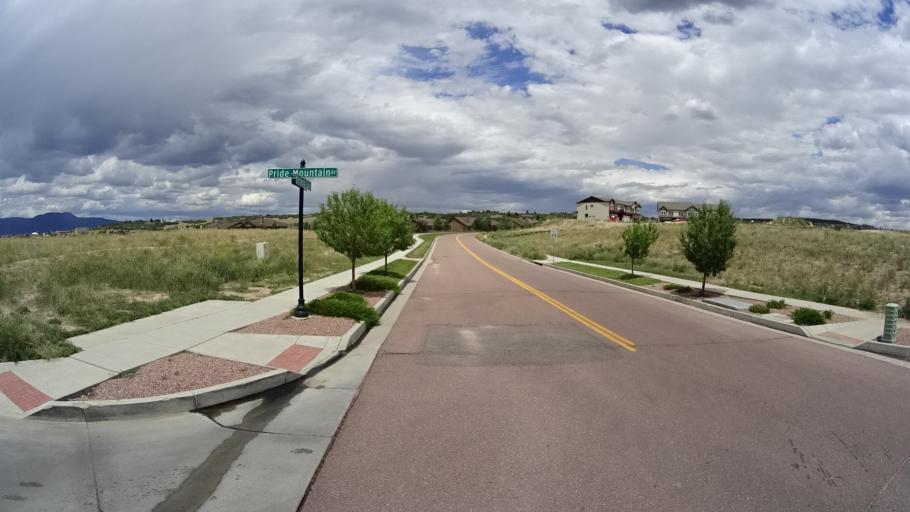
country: US
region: Colorado
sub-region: El Paso County
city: Gleneagle
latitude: 39.0235
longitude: -104.8001
